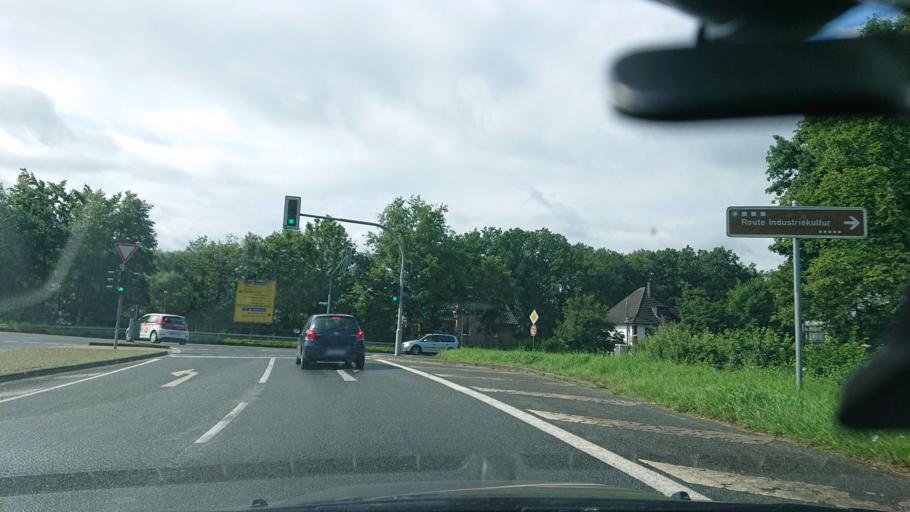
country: DE
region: North Rhine-Westphalia
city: Lunen
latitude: 51.6121
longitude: 7.5513
